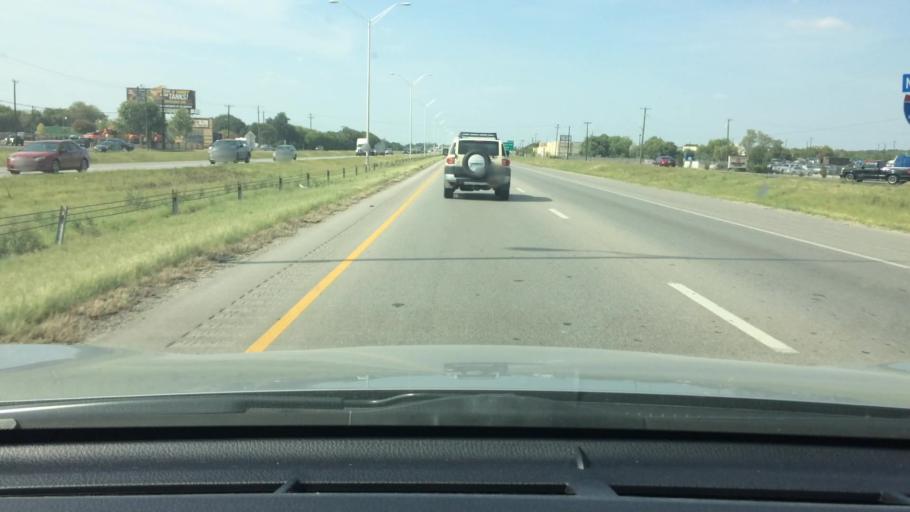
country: US
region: Texas
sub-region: Bexar County
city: China Grove
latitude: 29.3787
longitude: -98.3927
